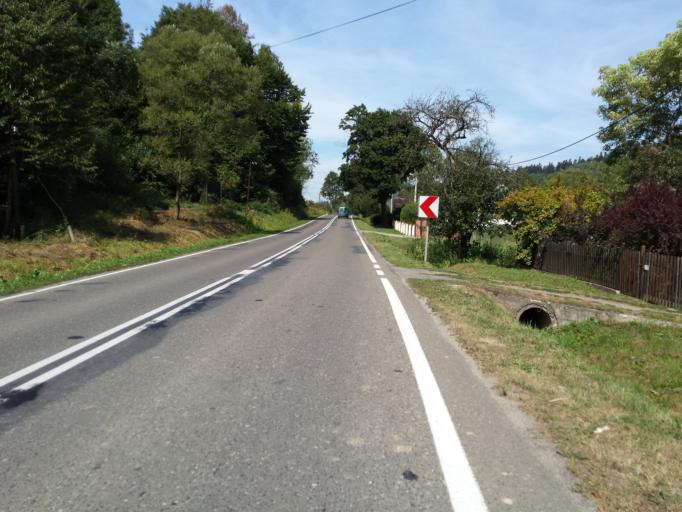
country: PL
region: Subcarpathian Voivodeship
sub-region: Powiat leski
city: Lesko
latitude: 49.4481
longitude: 22.3477
